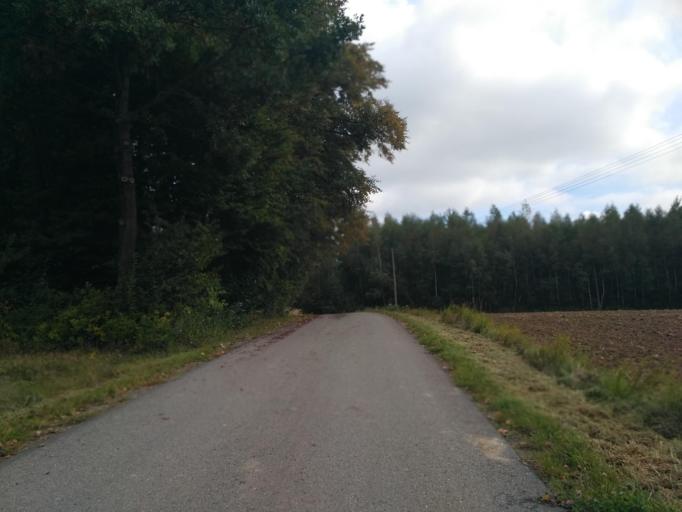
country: PL
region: Subcarpathian Voivodeship
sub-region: Powiat ropczycko-sedziszowski
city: Niedzwiada
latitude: 49.9200
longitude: 21.4907
